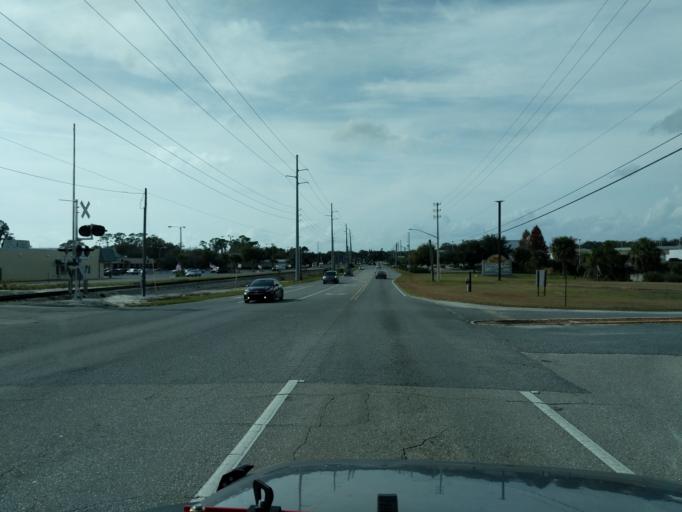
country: US
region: Florida
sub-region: Lake County
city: Mount Dora
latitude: 28.8076
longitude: -81.6707
